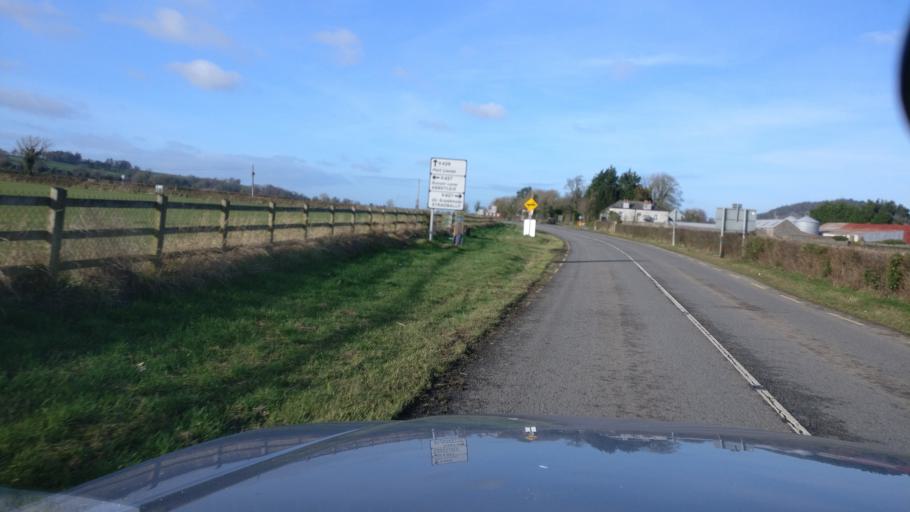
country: IE
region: Leinster
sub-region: Laois
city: Stradbally
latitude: 52.9947
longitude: -7.2215
